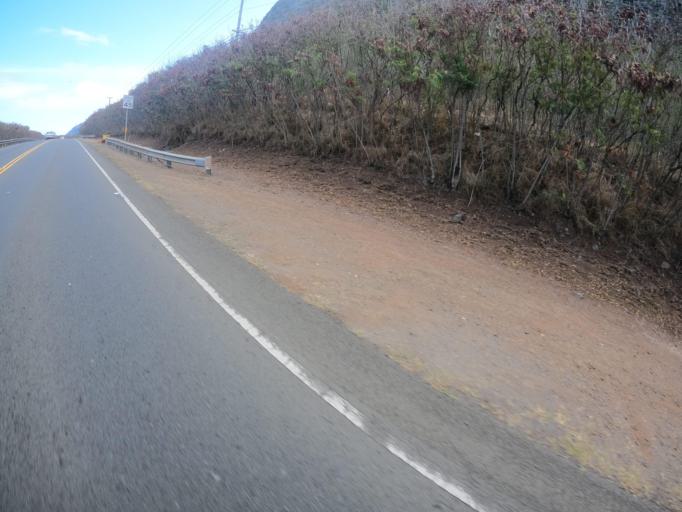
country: US
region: Hawaii
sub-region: Honolulu County
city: Waimanalo Beach
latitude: 21.3222
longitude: -157.6754
